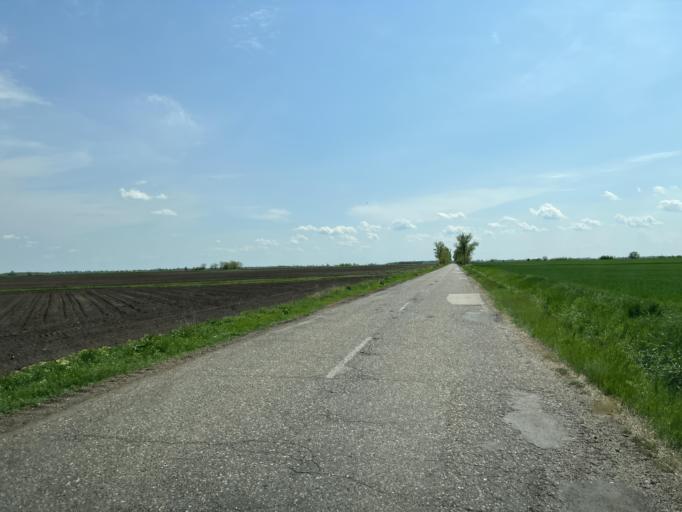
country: HU
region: Pest
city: Tapioszentmarton
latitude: 47.2884
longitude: 19.7623
